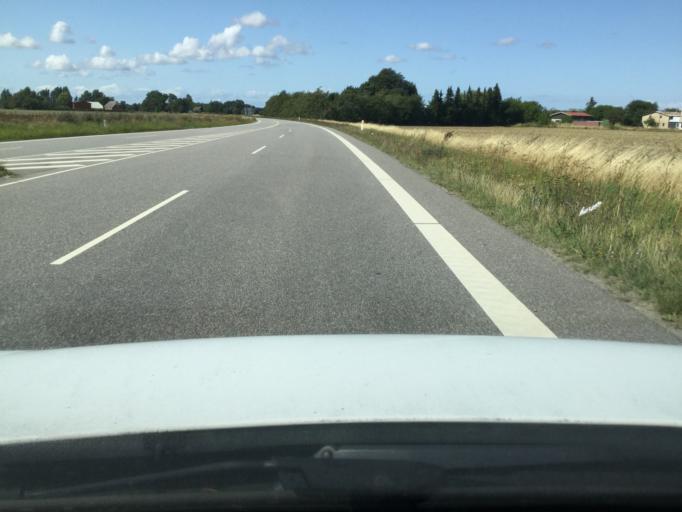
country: DK
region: Zealand
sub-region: Lolland Kommune
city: Rodby
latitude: 54.7471
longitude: 11.3862
